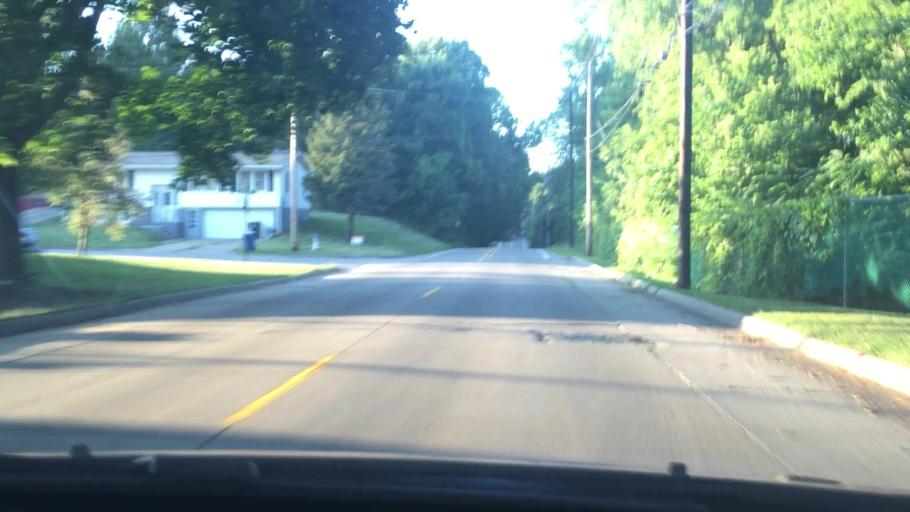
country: US
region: Iowa
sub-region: Muscatine County
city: Muscatine
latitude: 41.4259
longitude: -91.0649
